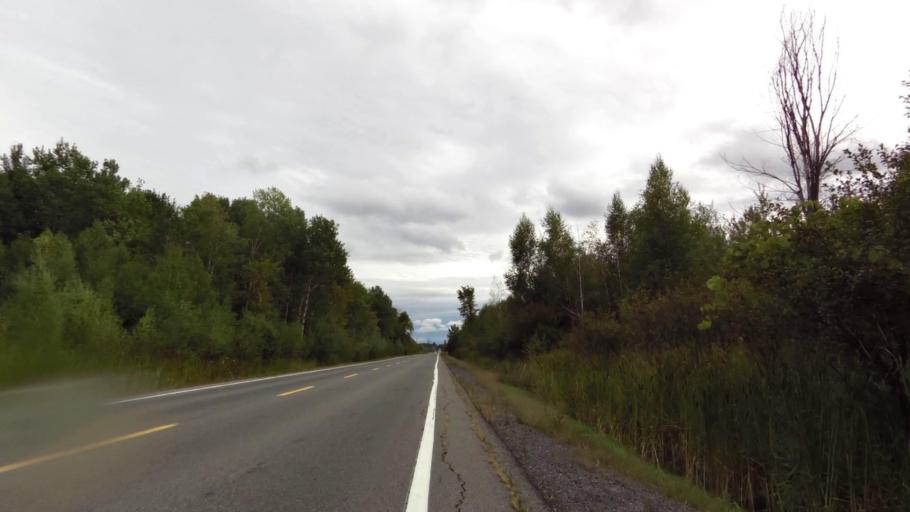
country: CA
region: Ontario
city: Ottawa
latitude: 45.3005
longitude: -75.6401
